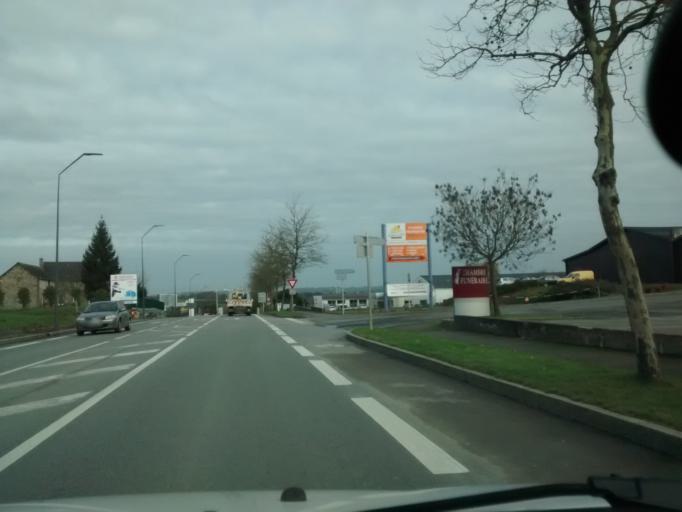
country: FR
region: Brittany
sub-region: Departement d'Ille-et-Vilaine
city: Vitre
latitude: 48.1202
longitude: -1.1872
